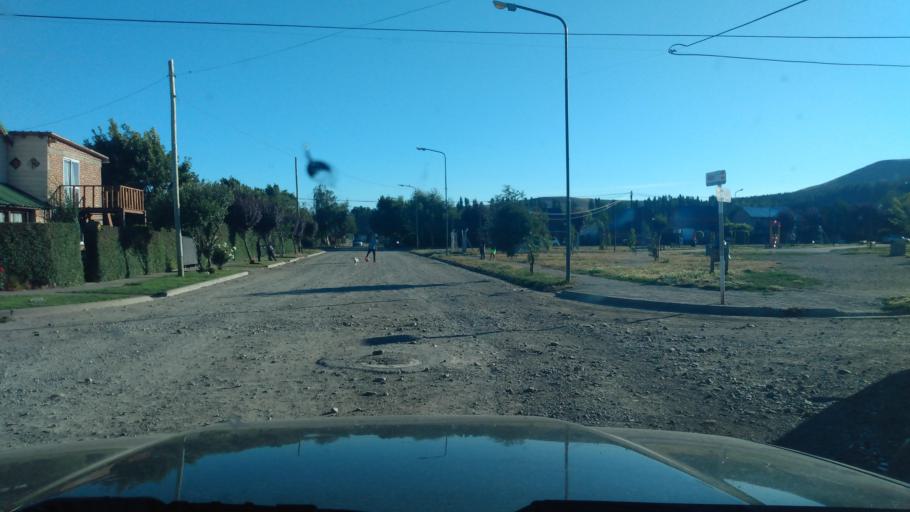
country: AR
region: Neuquen
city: Junin de los Andes
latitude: -39.9527
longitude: -71.0782
